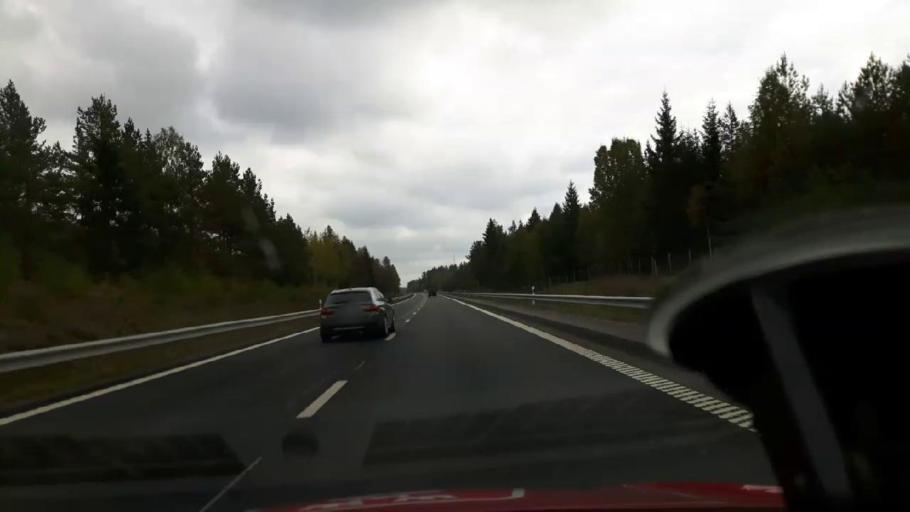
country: SE
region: Gaevleborg
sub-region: Gavle Kommun
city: Gavle
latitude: 60.6210
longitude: 17.1593
